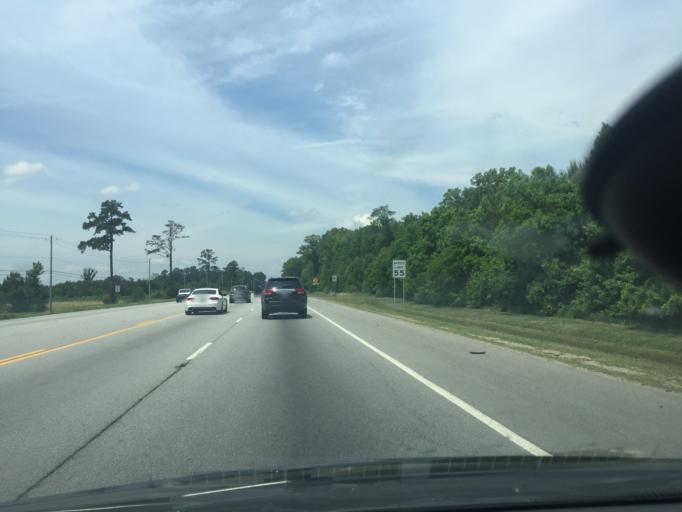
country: US
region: Georgia
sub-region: Chatham County
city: Bloomingdale
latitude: 32.1364
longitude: -81.3115
